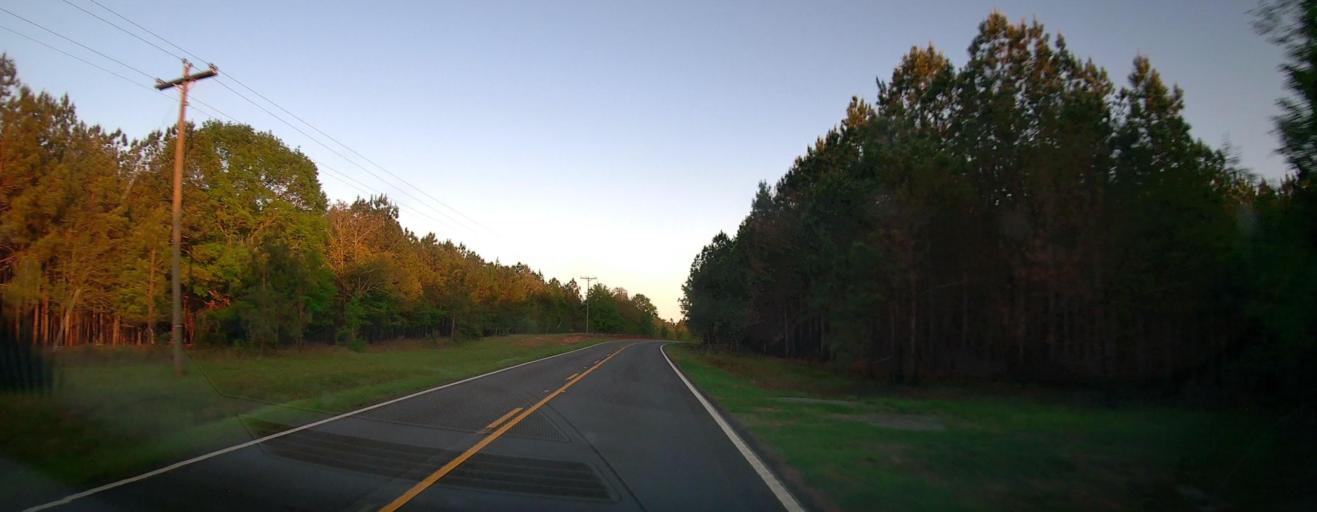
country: US
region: Georgia
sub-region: Marion County
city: Buena Vista
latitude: 32.3907
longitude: -84.5679
